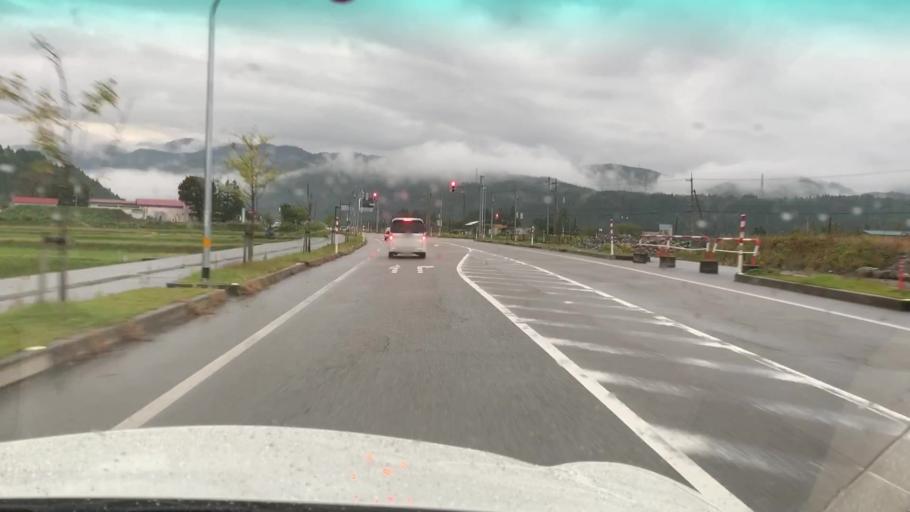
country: JP
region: Toyama
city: Kamiichi
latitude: 36.5949
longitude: 137.3274
